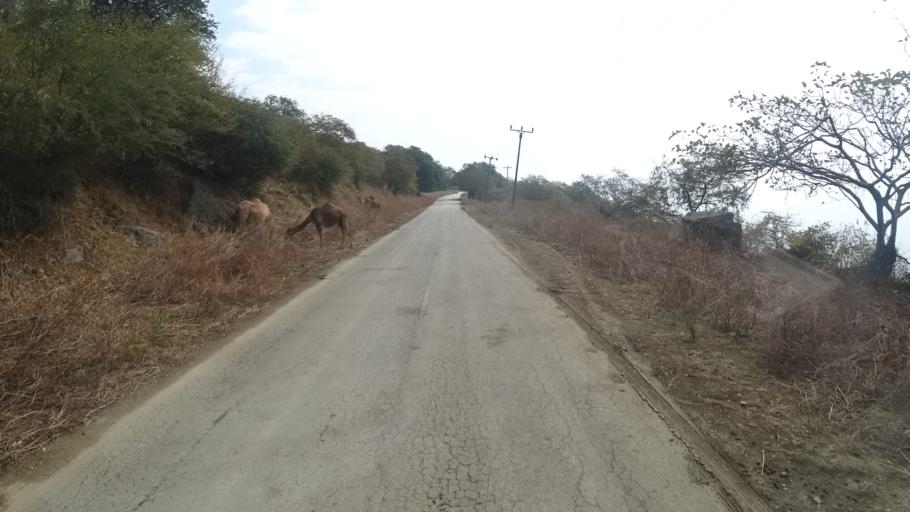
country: YE
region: Al Mahrah
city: Hawf
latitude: 16.7112
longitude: 53.2321
